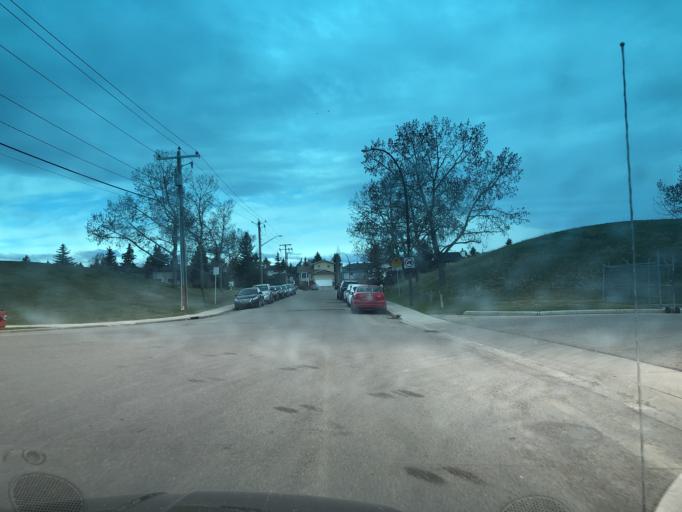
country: CA
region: Alberta
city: Calgary
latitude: 51.0707
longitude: -114.0088
